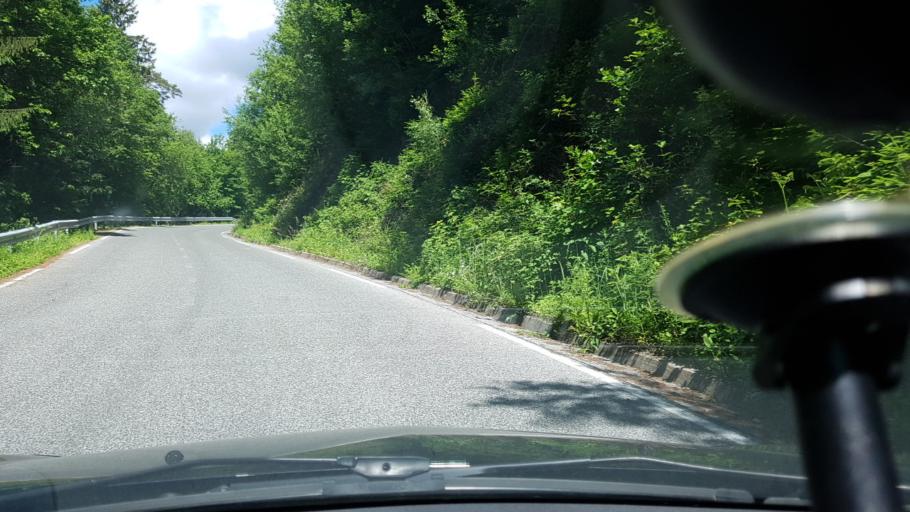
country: SI
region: Zrece
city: Zrece
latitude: 46.4145
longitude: 15.3676
